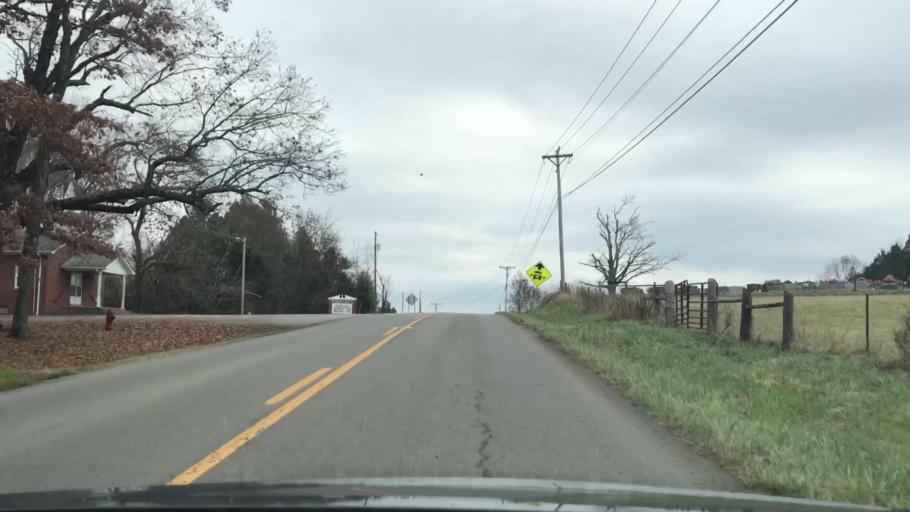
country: US
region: Kentucky
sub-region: Metcalfe County
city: Edmonton
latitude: 36.9357
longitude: -85.6319
